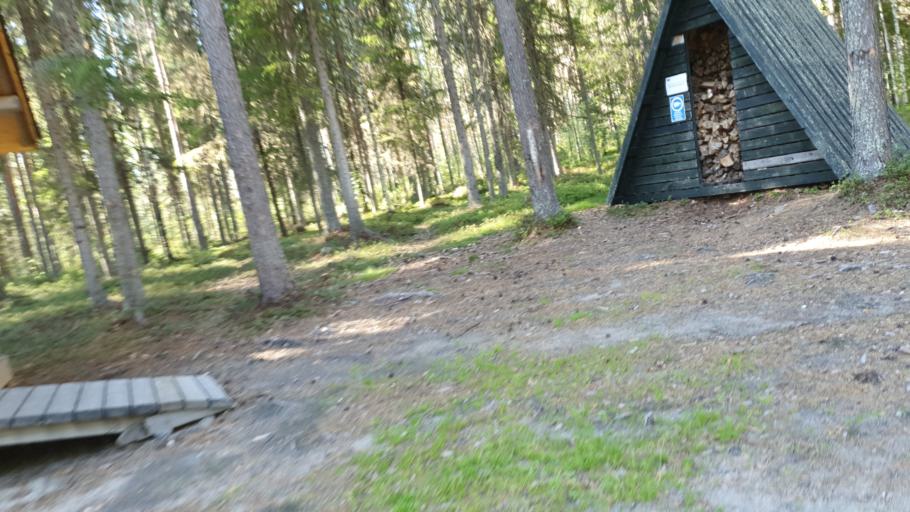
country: FI
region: Kainuu
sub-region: Kehys-Kainuu
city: Kuhmo
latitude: 64.1081
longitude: 29.5077
